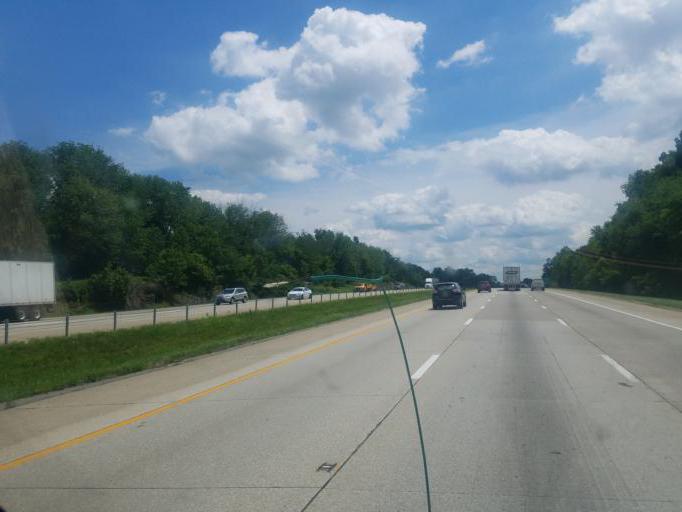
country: US
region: Kentucky
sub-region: Bullitt County
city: Shepherdsville
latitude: 38.0168
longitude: -85.6968
